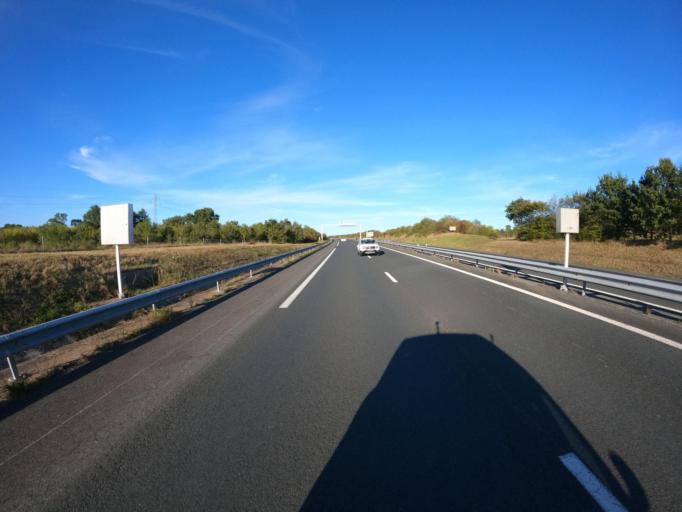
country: FR
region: Pays de la Loire
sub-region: Departement de Maine-et-Loire
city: Mazieres-en-Mauges
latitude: 47.0374
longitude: -0.8483
